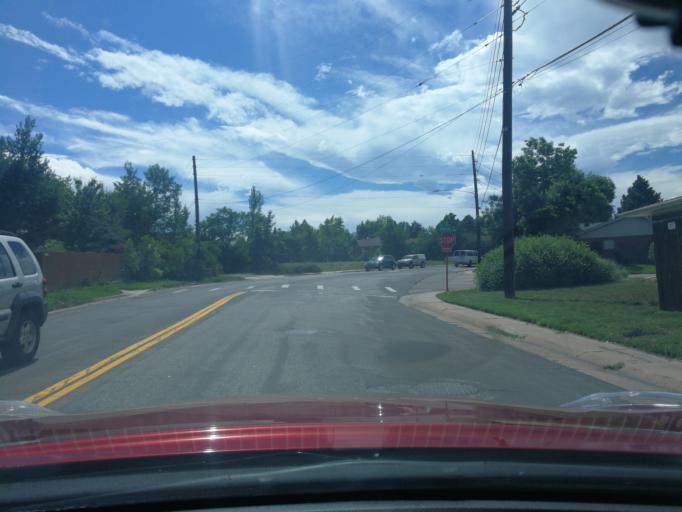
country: US
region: Colorado
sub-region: Arapahoe County
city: Littleton
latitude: 39.5898
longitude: -104.9931
